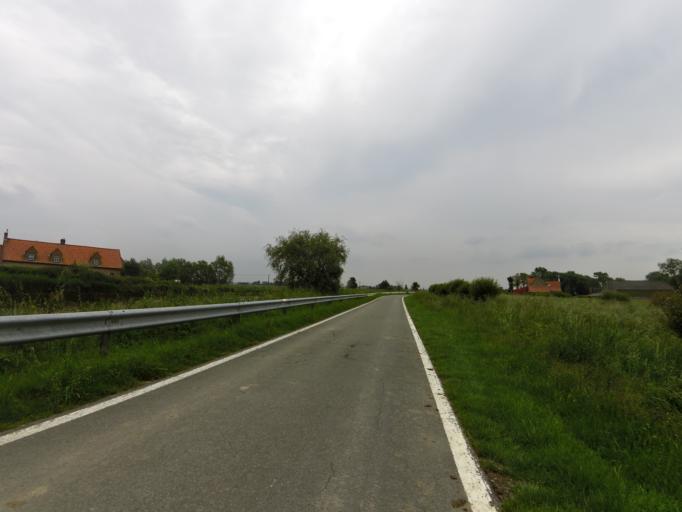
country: BE
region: Flanders
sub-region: Provincie West-Vlaanderen
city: Middelkerke
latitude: 51.1131
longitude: 2.8235
